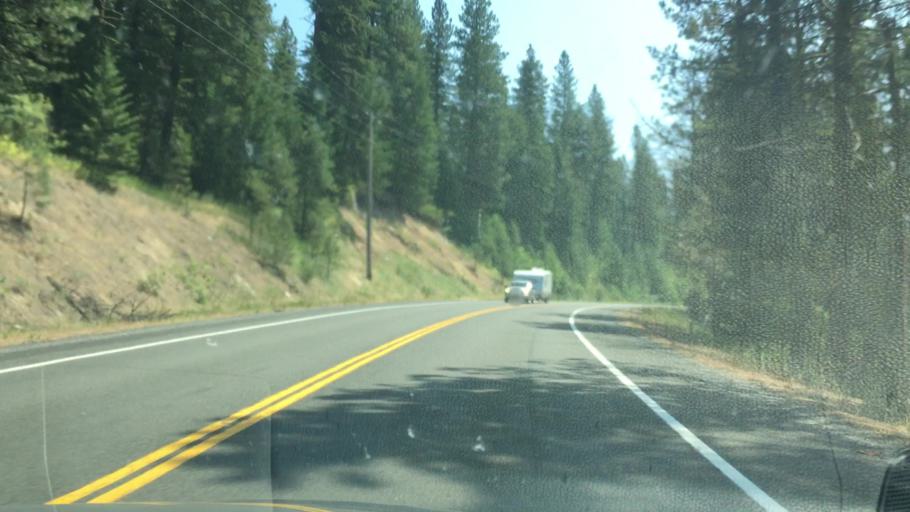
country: US
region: Idaho
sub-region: Valley County
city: McCall
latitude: 45.1124
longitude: -116.3020
